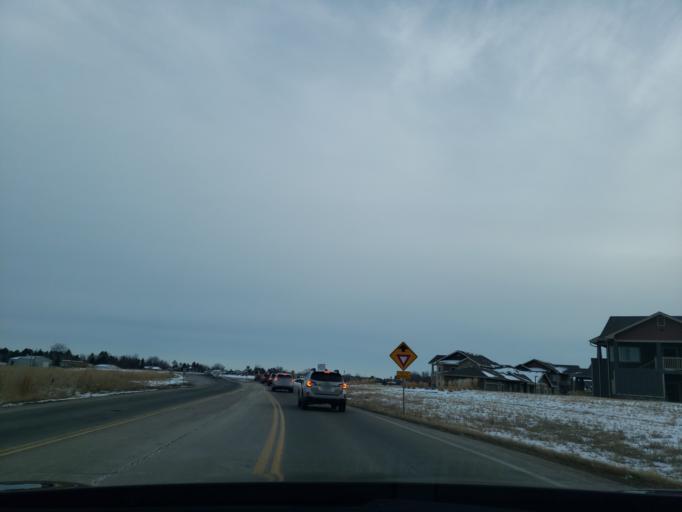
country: US
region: Colorado
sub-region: Larimer County
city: Campion
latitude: 40.3480
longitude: -105.0968
